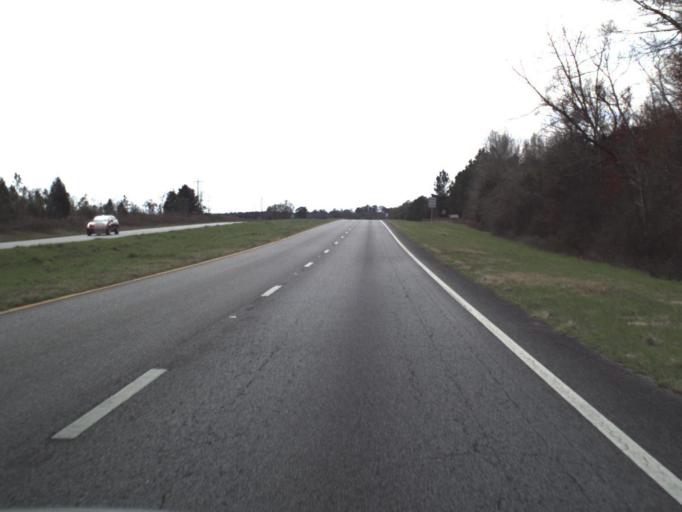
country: US
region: Florida
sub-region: Jackson County
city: Marianna
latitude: 30.8174
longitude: -85.3690
